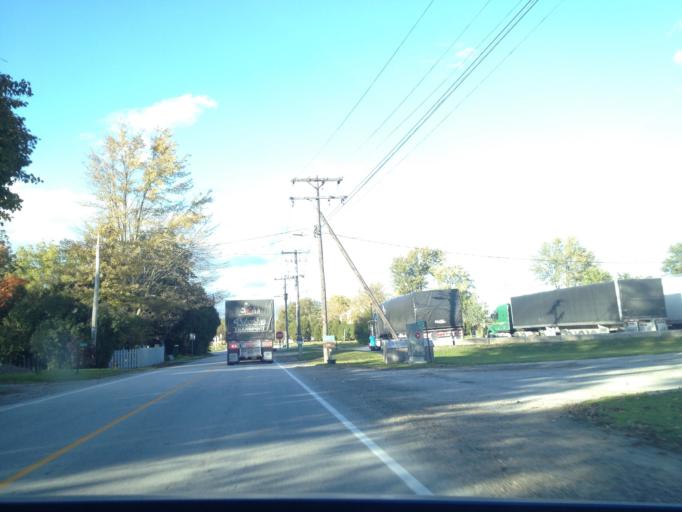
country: US
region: Michigan
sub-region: Wayne County
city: Grosse Pointe
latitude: 42.2132
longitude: -82.7159
